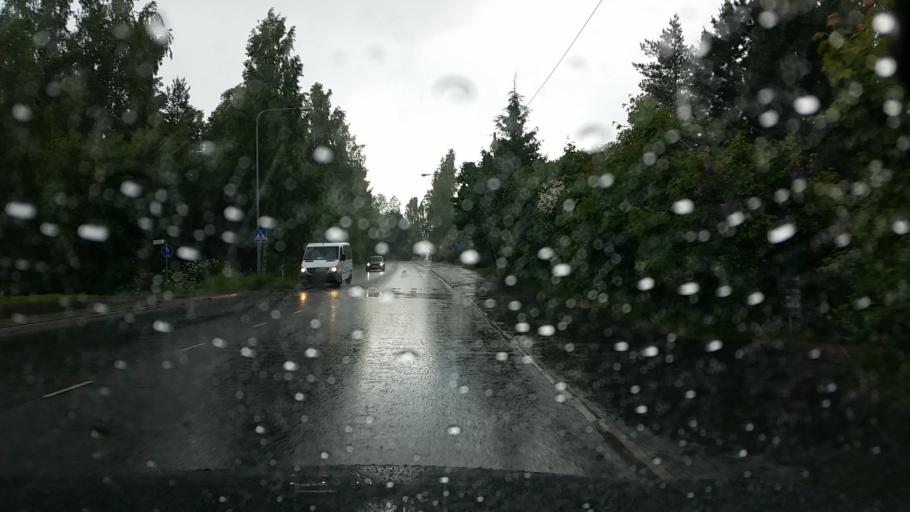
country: FI
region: Uusimaa
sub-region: Helsinki
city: Teekkarikylae
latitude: 60.2577
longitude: 24.8724
